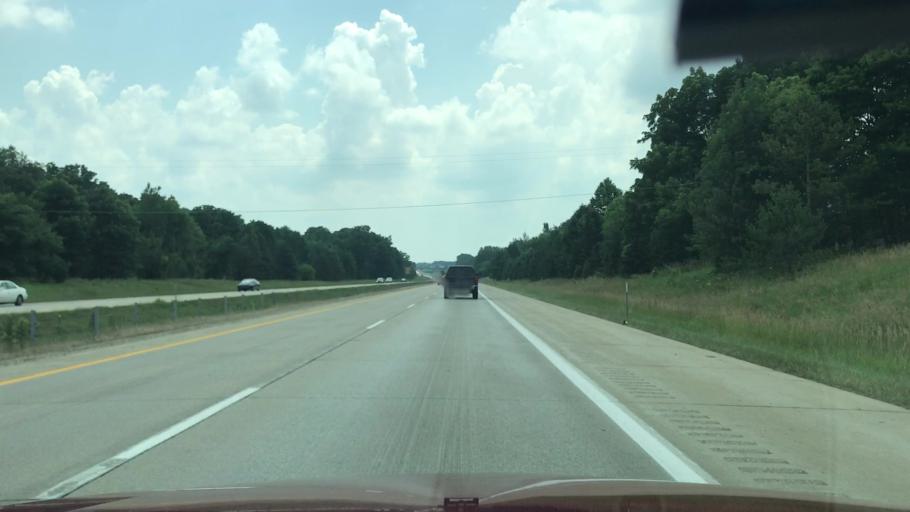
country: US
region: Michigan
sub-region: Allegan County
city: Plainwell
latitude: 42.4797
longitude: -85.6527
